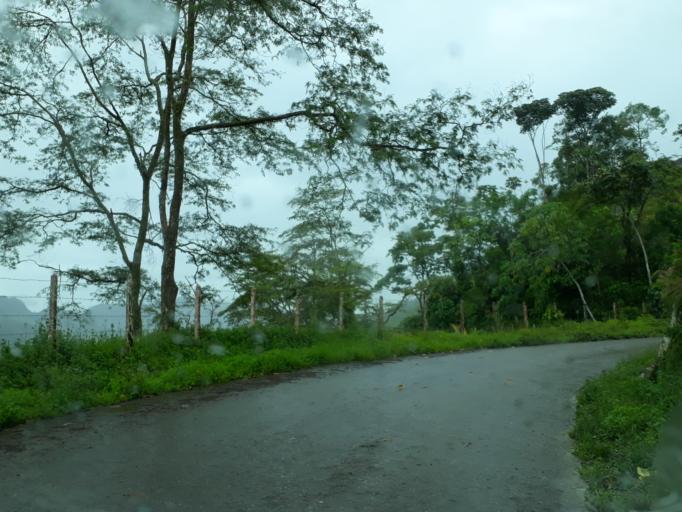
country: CO
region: Boyaca
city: Santa Maria
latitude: 4.7040
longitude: -73.3015
